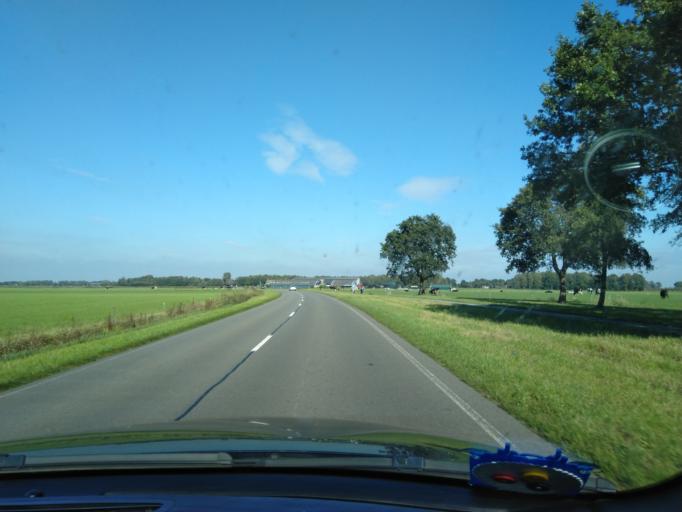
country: NL
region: Drenthe
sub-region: Gemeente Aa en Hunze
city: Anloo
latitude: 53.0665
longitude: 6.7577
